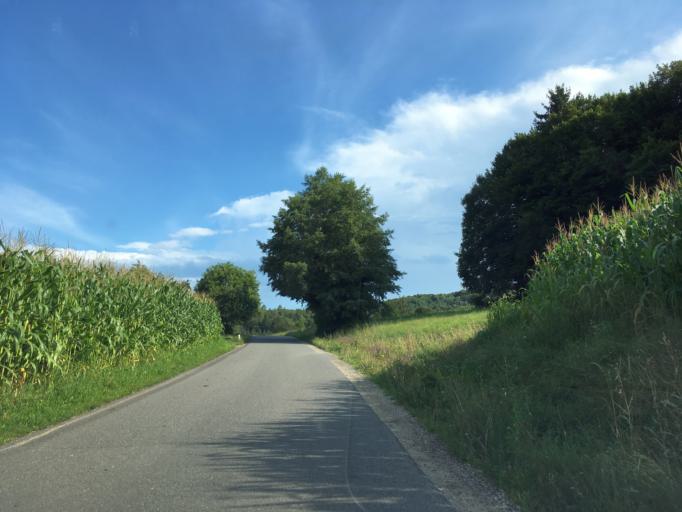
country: AT
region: Styria
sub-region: Politischer Bezirk Leibnitz
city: Sankt Nikolai im Sausal
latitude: 46.8125
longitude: 15.4545
